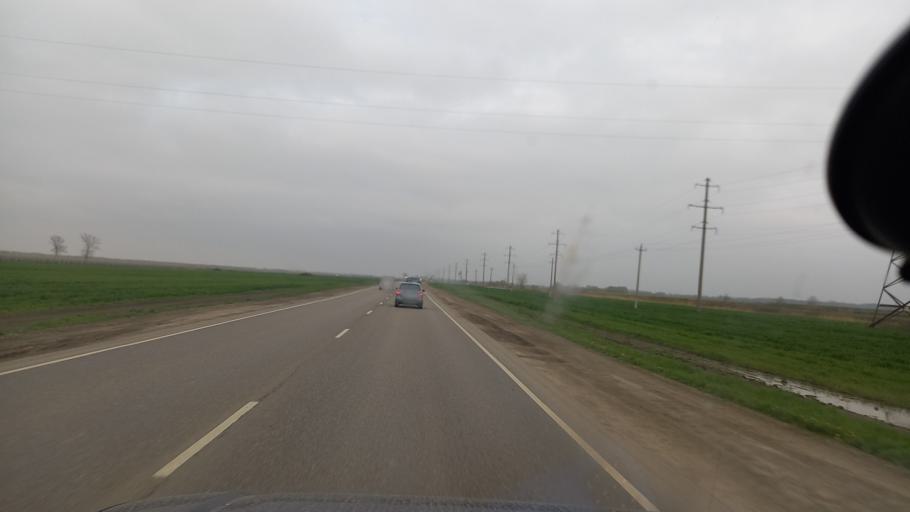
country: RU
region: Krasnodarskiy
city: Slavyansk-na-Kubani
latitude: 45.2394
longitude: 38.0157
